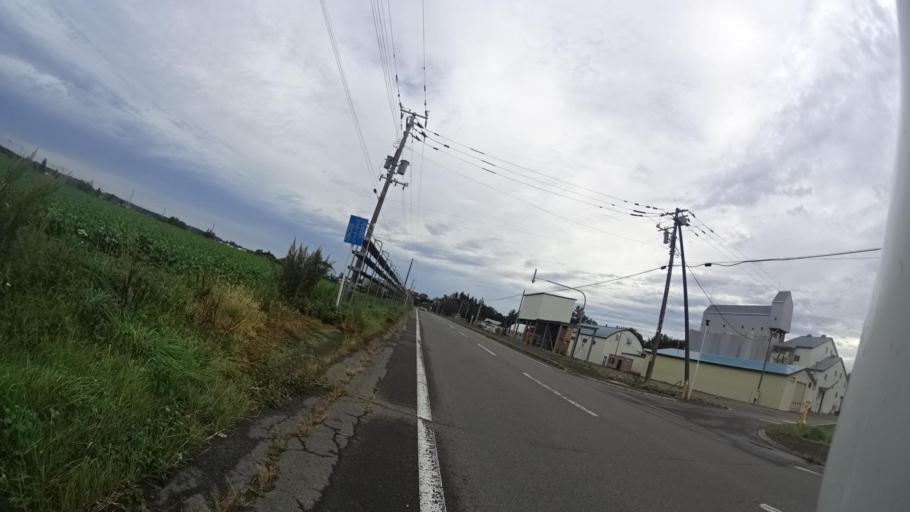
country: JP
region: Hokkaido
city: Abashiri
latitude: 43.8459
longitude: 144.5976
